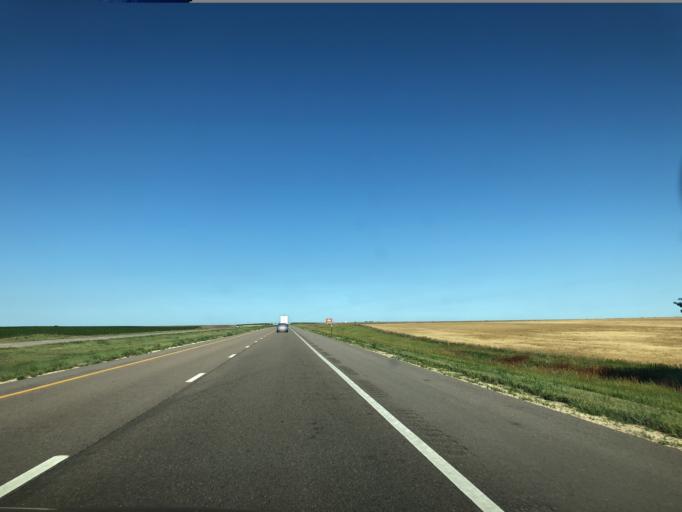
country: US
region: Kansas
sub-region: Sherman County
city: Goodland
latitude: 39.3300
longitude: -101.5714
